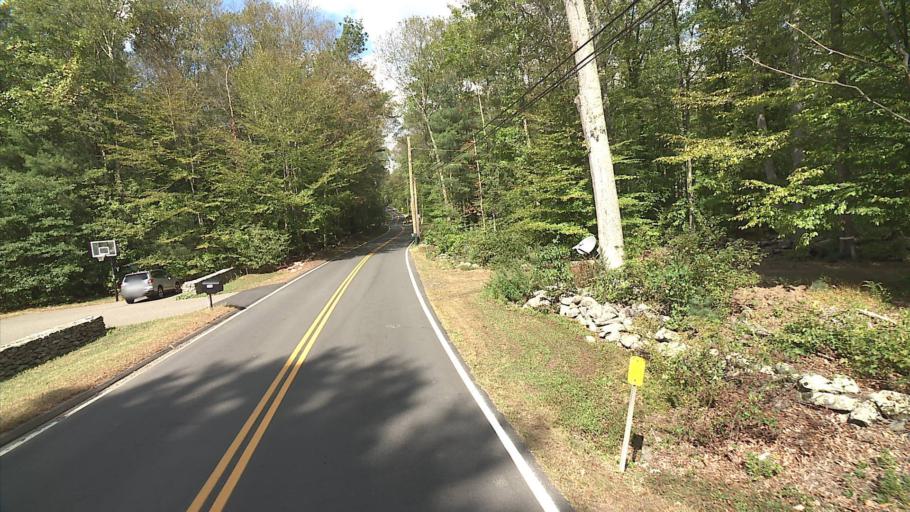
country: US
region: Connecticut
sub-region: New Haven County
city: Madison
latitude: 41.3852
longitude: -72.5939
